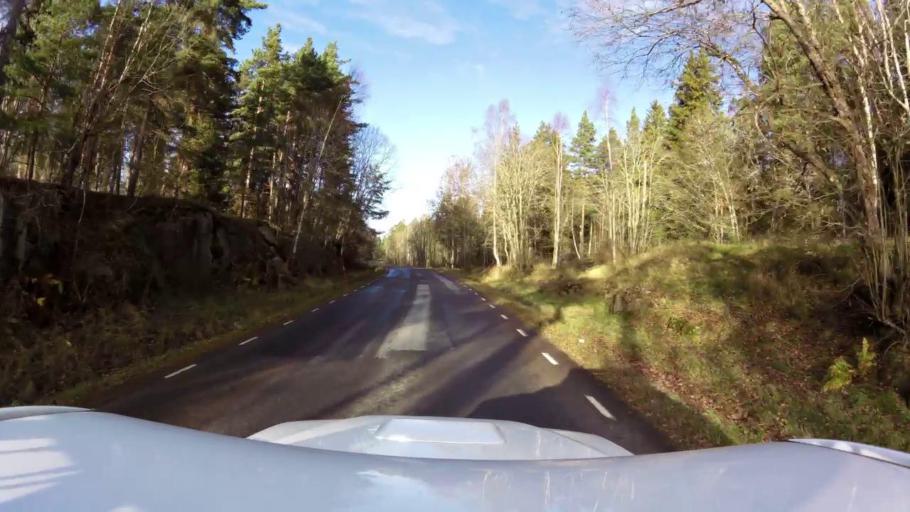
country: SE
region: OEstergoetland
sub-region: Linkopings Kommun
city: Linkoping
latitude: 58.3730
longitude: 15.6263
